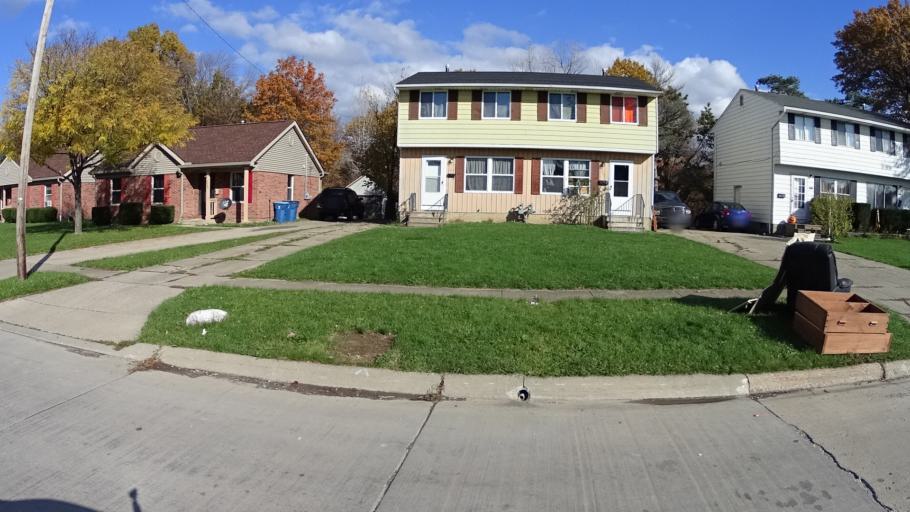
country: US
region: Ohio
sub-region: Lorain County
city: Sheffield
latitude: 41.4272
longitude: -82.1063
